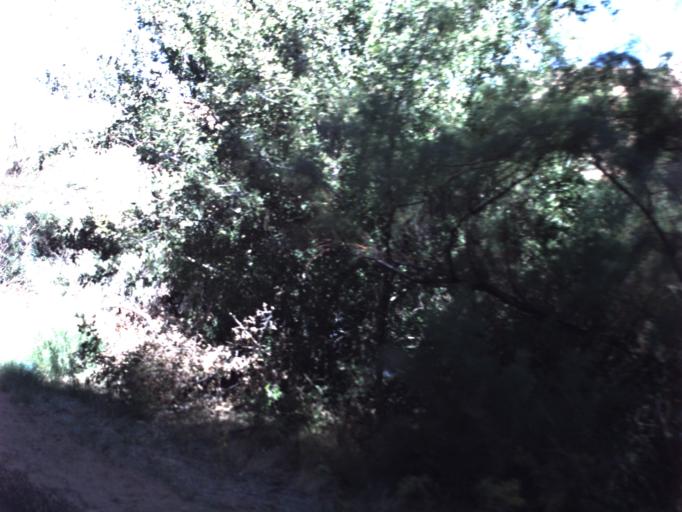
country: US
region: Utah
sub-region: Grand County
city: Moab
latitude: 38.5451
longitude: -109.5999
